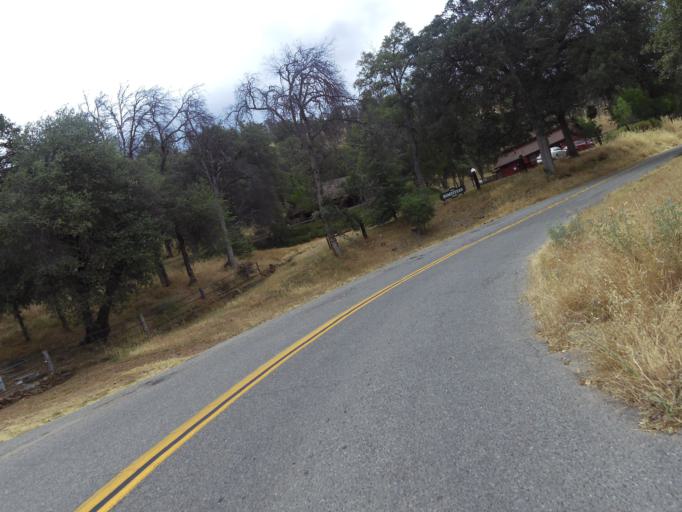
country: US
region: California
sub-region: Madera County
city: Ahwahnee
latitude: 37.3487
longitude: -119.7606
